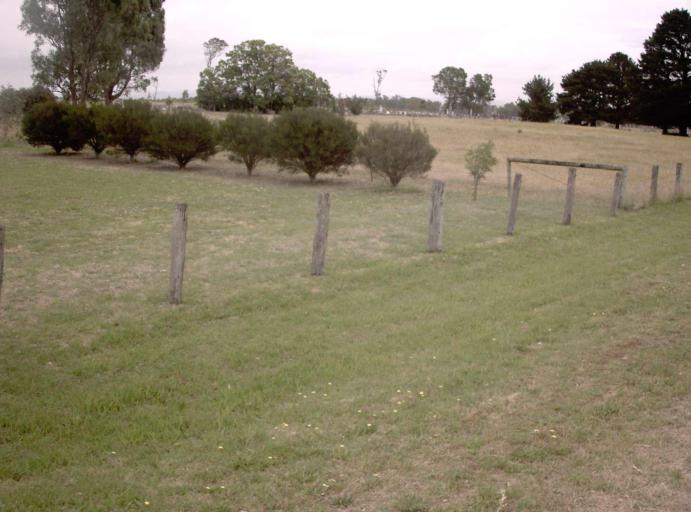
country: AU
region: Victoria
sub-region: East Gippsland
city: Bairnsdale
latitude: -37.8226
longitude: 147.4351
